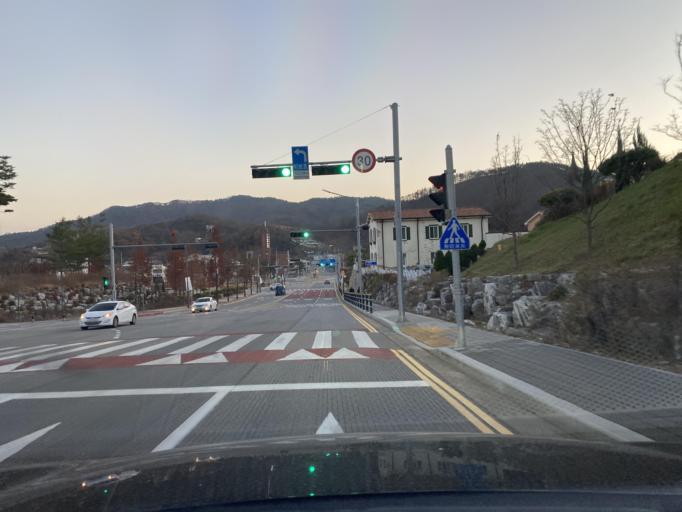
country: KR
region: Chungcheongnam-do
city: Yesan
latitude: 36.6807
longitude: 126.8434
